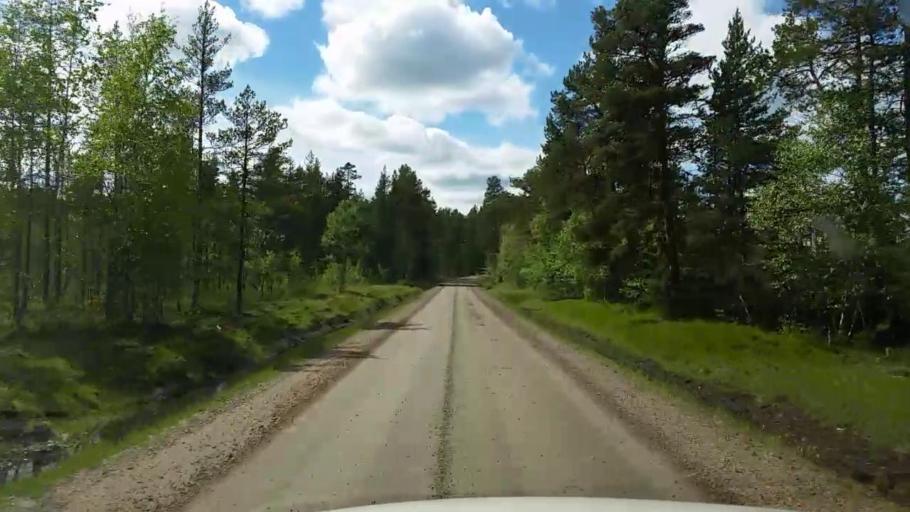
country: SE
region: Gaevleborg
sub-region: Ovanakers Kommun
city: Edsbyn
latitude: 61.5712
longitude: 15.9399
